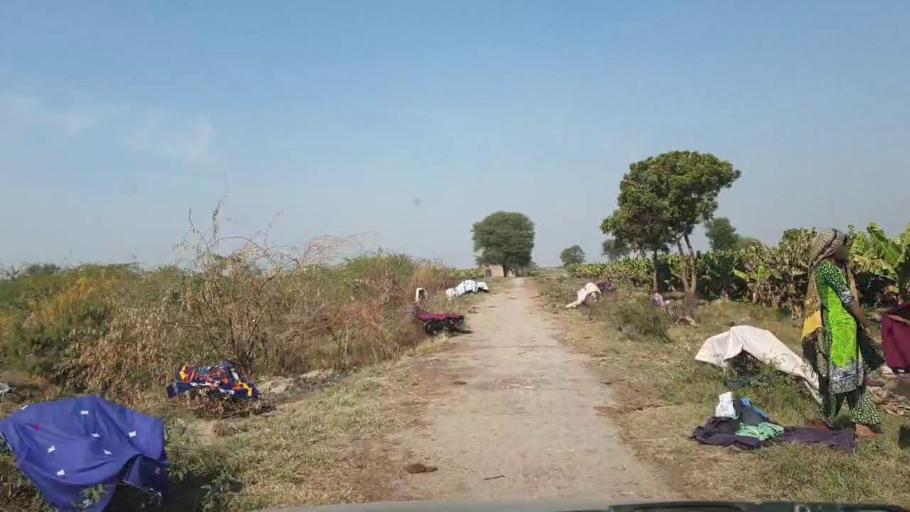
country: PK
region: Sindh
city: Chambar
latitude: 25.3237
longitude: 68.8056
